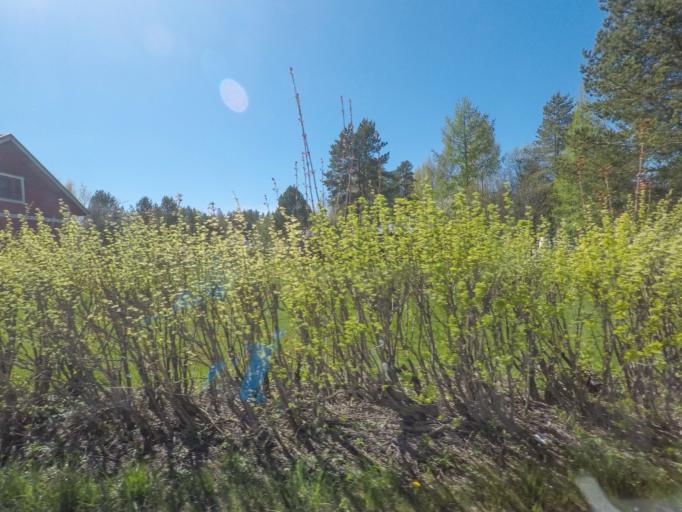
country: FI
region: Uusimaa
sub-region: Helsinki
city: Sammatti
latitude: 60.3228
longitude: 23.8177
